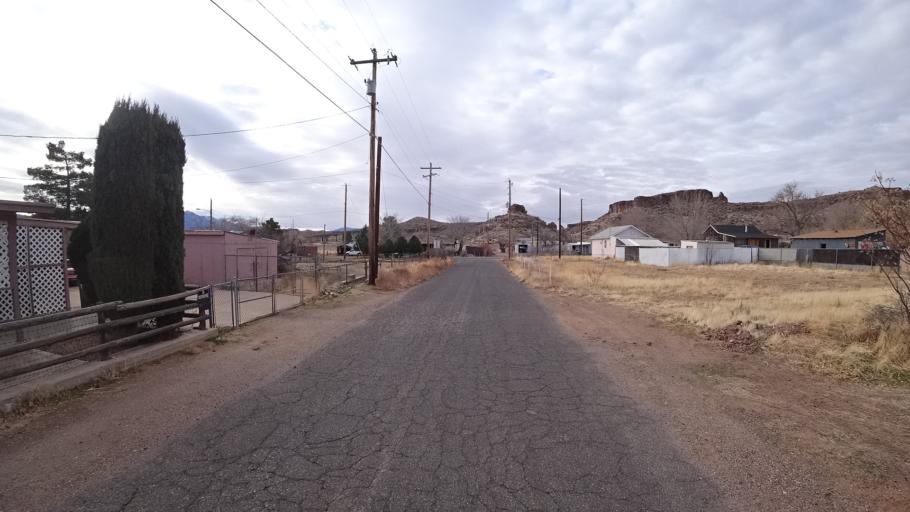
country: US
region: Arizona
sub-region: Mohave County
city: Kingman
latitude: 35.2154
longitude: -114.0533
